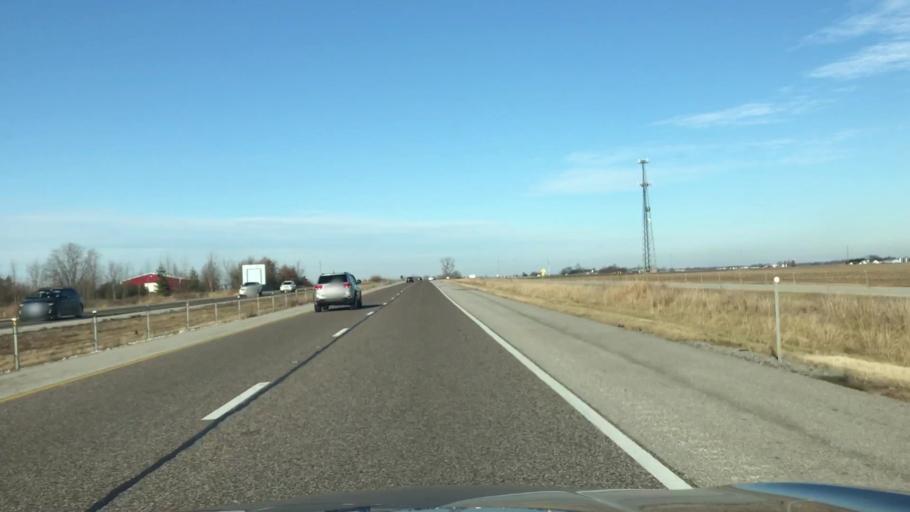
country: US
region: Illinois
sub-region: Madison County
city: Edwardsville
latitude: 38.8111
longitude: -89.8909
